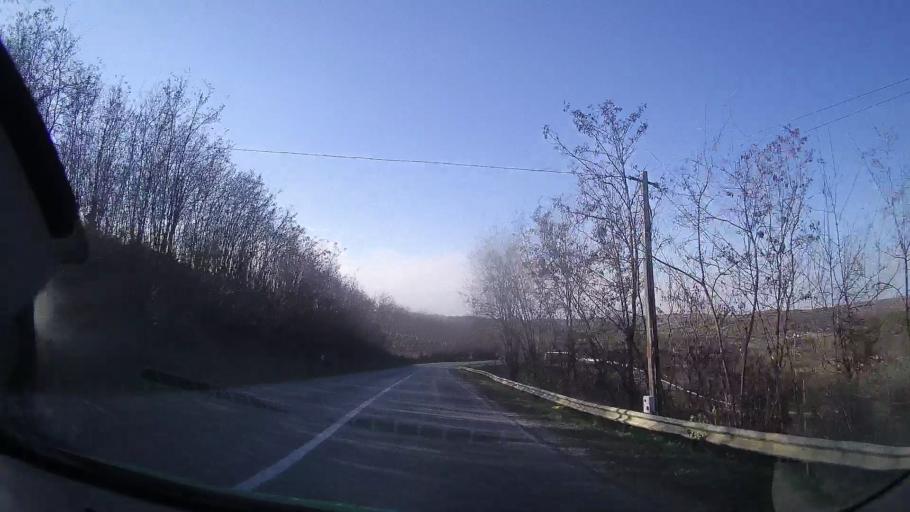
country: RO
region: Cluj
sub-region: Comuna Mociu
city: Mociu
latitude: 46.8006
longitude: 24.0466
